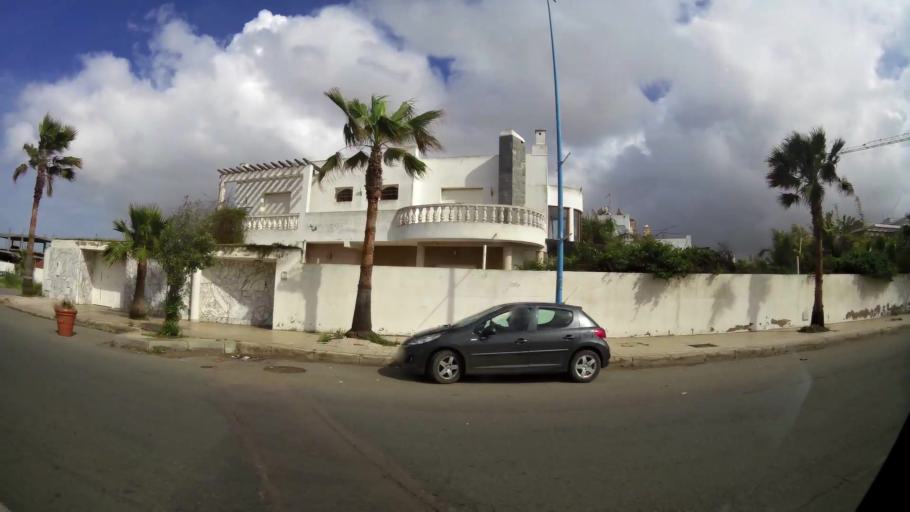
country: MA
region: Grand Casablanca
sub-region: Casablanca
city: Casablanca
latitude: 33.5724
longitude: -7.7075
